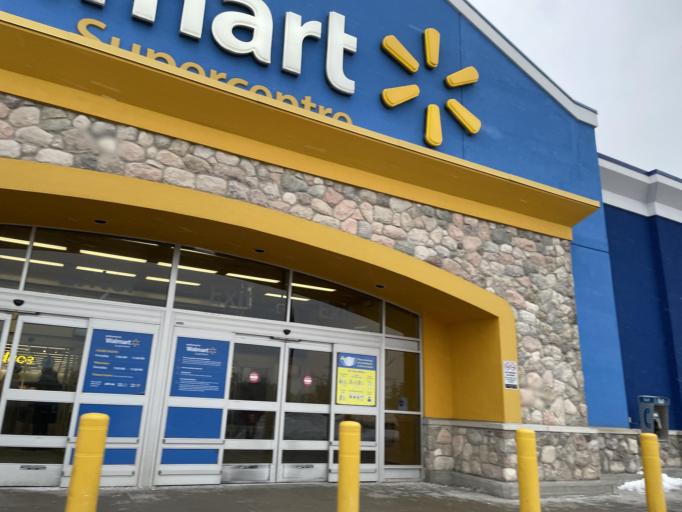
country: CA
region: Ontario
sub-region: Wellington County
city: Guelph
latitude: 43.5653
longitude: -80.2811
